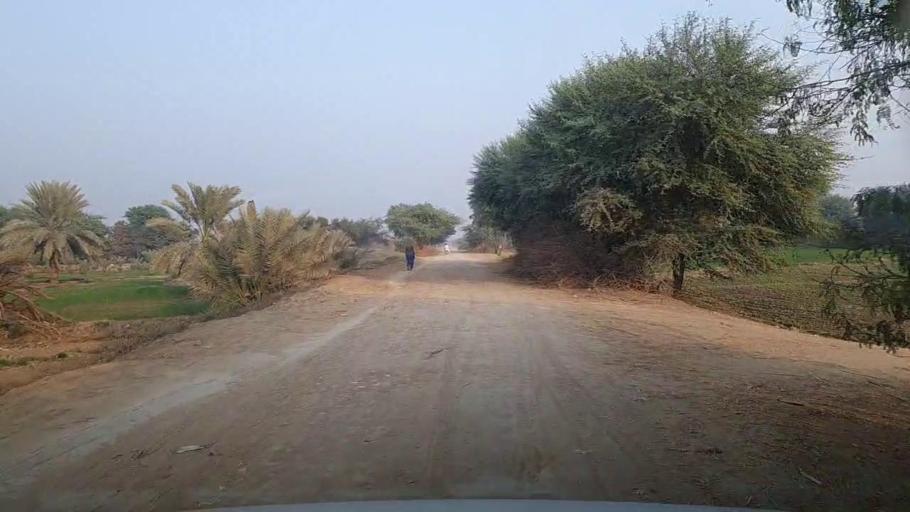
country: PK
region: Sindh
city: Bozdar
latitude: 27.0827
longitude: 68.5455
